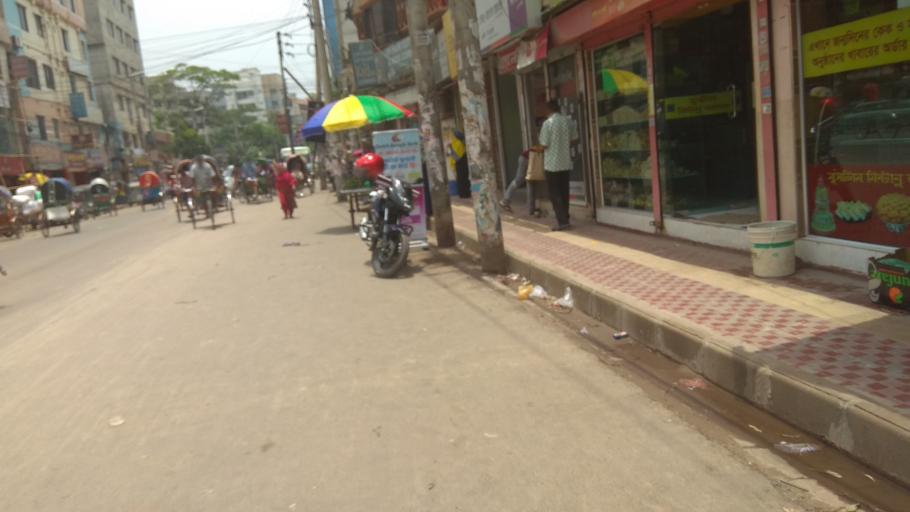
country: BD
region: Dhaka
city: Tungi
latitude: 23.8165
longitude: 90.3560
